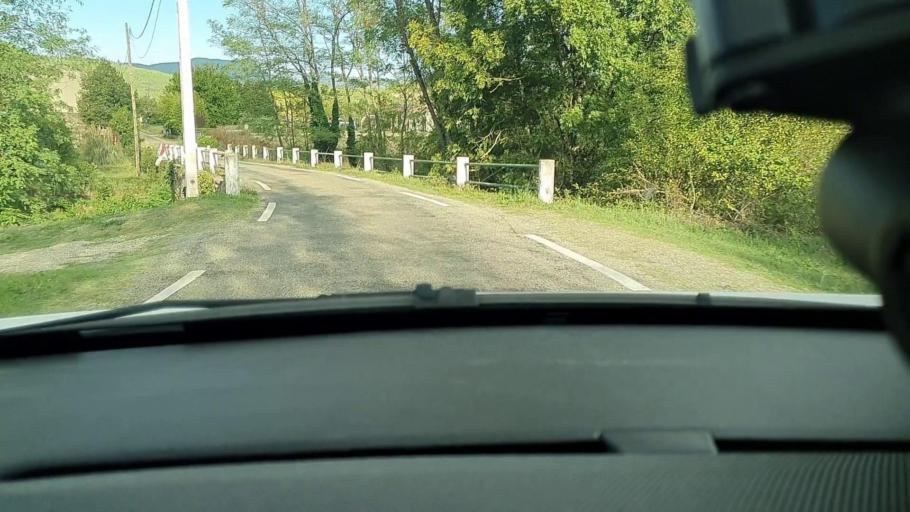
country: FR
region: Languedoc-Roussillon
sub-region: Departement du Gard
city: Besseges
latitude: 44.3187
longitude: 4.1324
